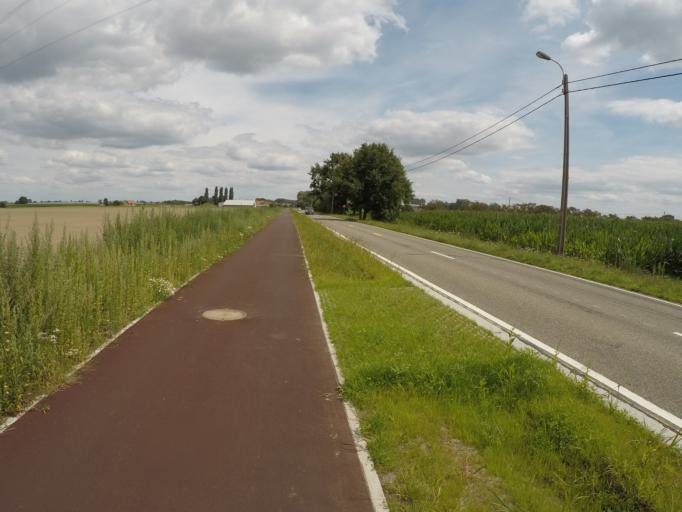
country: BE
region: Flanders
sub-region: Provincie Antwerpen
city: Ranst
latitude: 51.1731
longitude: 4.5661
